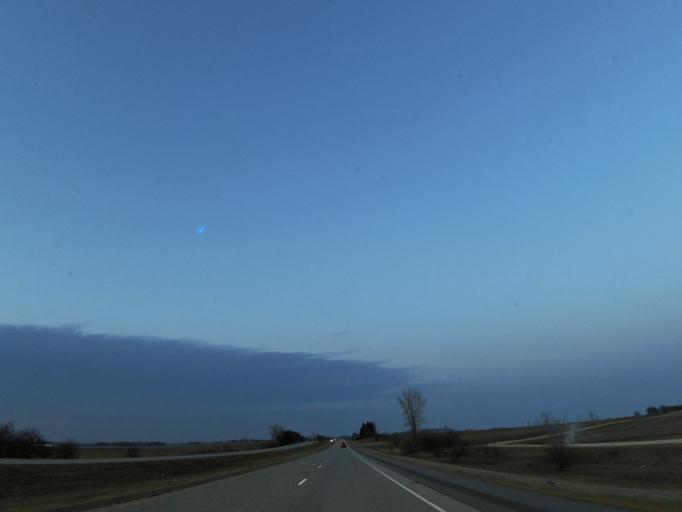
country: US
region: Minnesota
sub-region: Mower County
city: Grand Meadow
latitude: 43.7894
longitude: -92.6083
